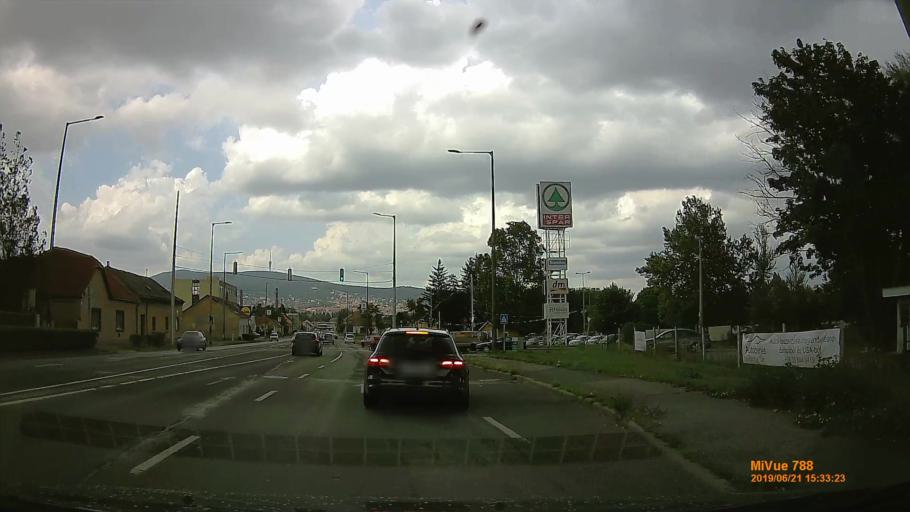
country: HU
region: Baranya
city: Pecs
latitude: 46.0553
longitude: 18.2311
